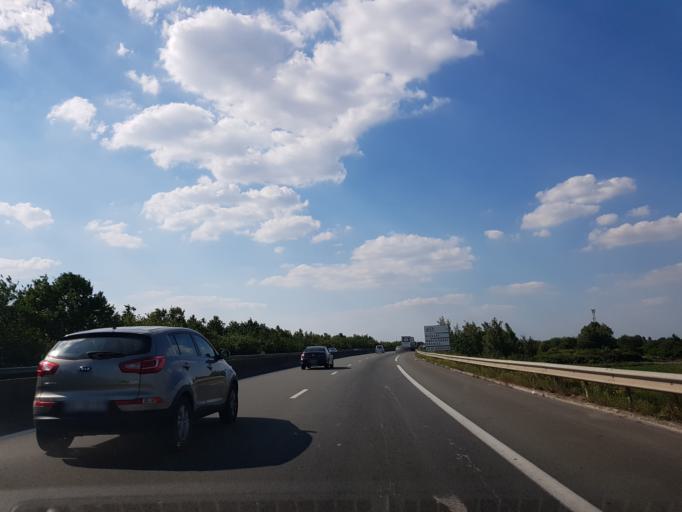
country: FR
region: Nord-Pas-de-Calais
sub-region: Departement du Nord
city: Somain
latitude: 50.3514
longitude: 3.2639
